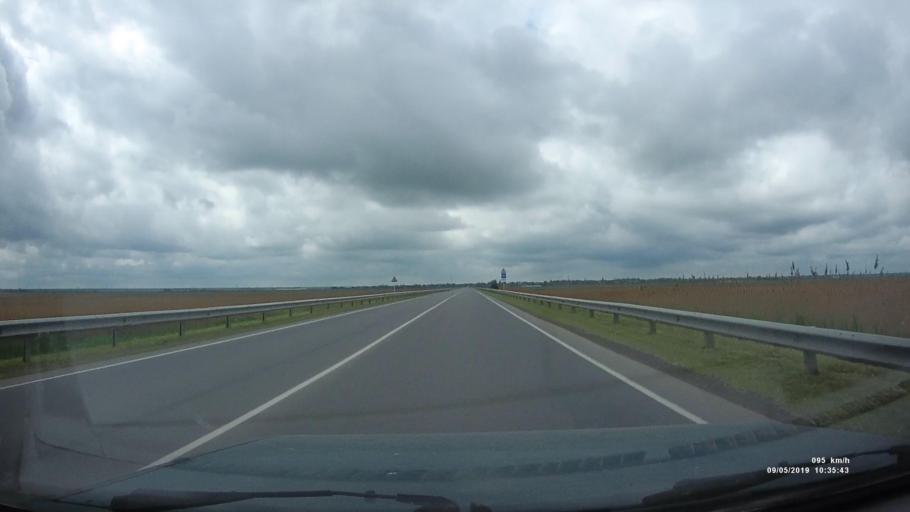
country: RU
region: Rostov
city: Peshkovo
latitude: 47.0388
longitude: 39.4121
